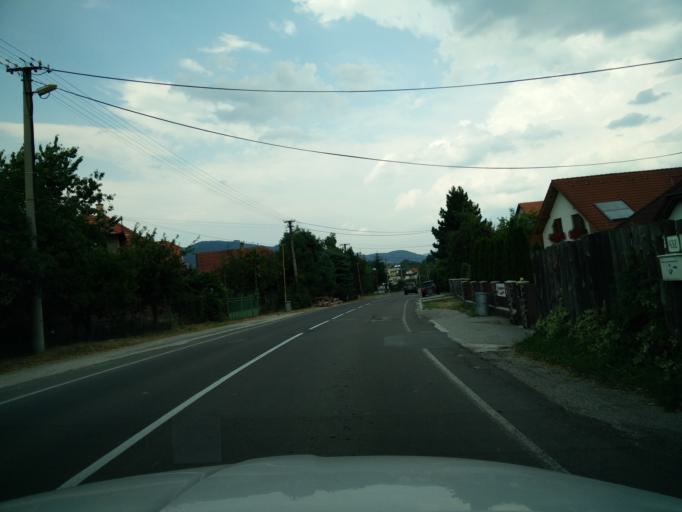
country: SK
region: Nitriansky
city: Novaky
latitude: 48.7900
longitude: 18.4776
